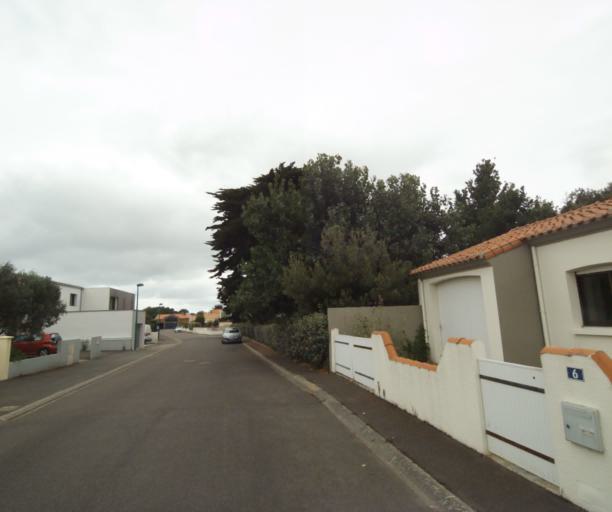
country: FR
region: Pays de la Loire
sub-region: Departement de la Vendee
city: Chateau-d'Olonne
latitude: 46.4900
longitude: -1.7559
